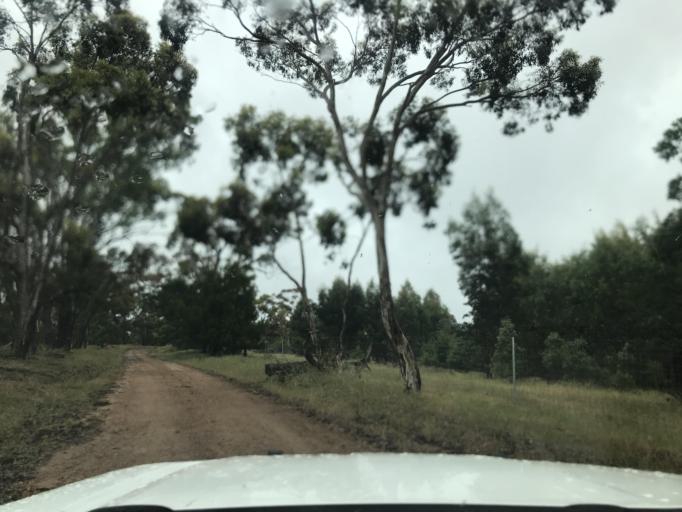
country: AU
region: South Australia
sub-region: Wattle Range
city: Penola
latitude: -37.2633
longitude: 141.3150
